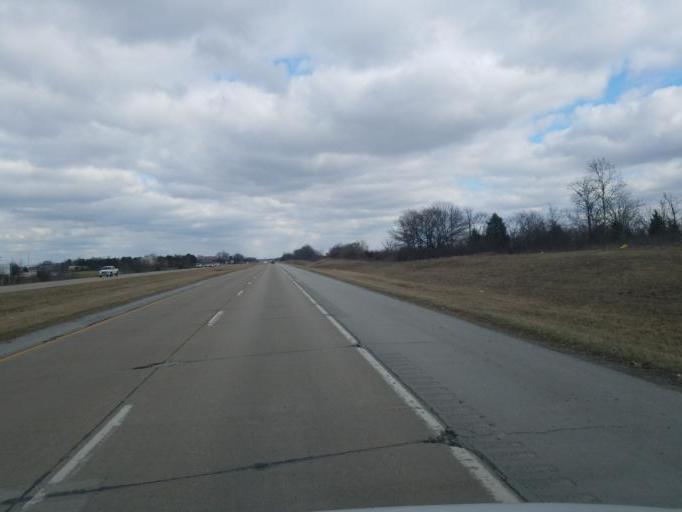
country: US
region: Indiana
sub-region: Hendricks County
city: Danville
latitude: 39.7568
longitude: -86.4783
